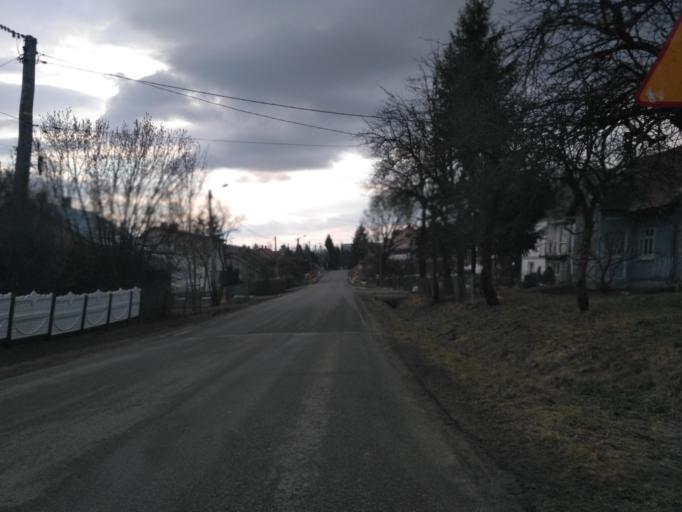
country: PL
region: Subcarpathian Voivodeship
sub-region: Powiat sanocki
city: Strachocina
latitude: 49.6113
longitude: 22.1454
